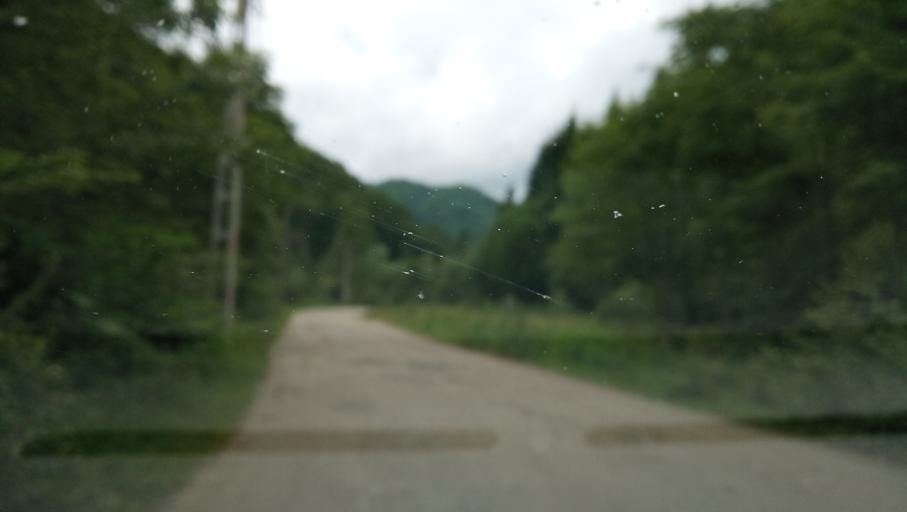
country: RO
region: Hunedoara
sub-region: Oras Petrila
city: Petrila
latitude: 45.4789
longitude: 23.4157
